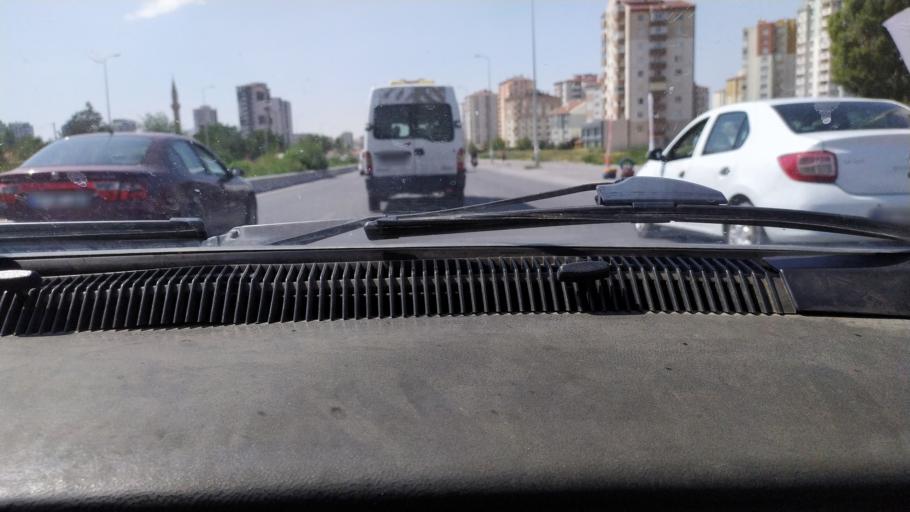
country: TR
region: Kayseri
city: Talas
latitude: 38.7213
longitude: 35.5388
